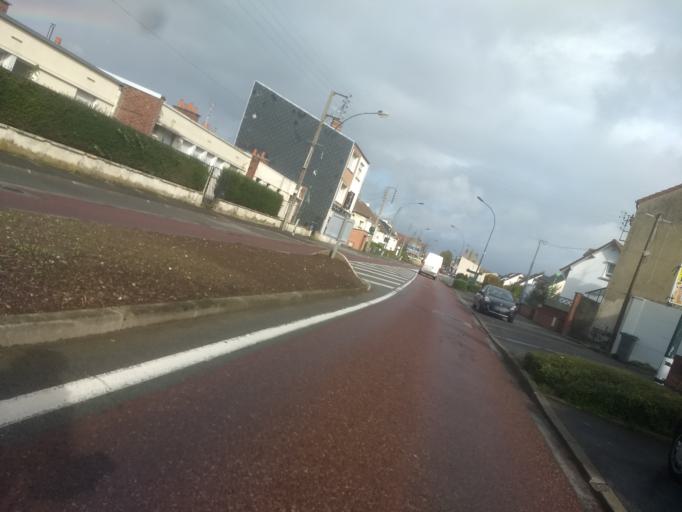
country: FR
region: Nord-Pas-de-Calais
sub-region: Departement du Pas-de-Calais
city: Achicourt
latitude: 50.2722
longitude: 2.7746
